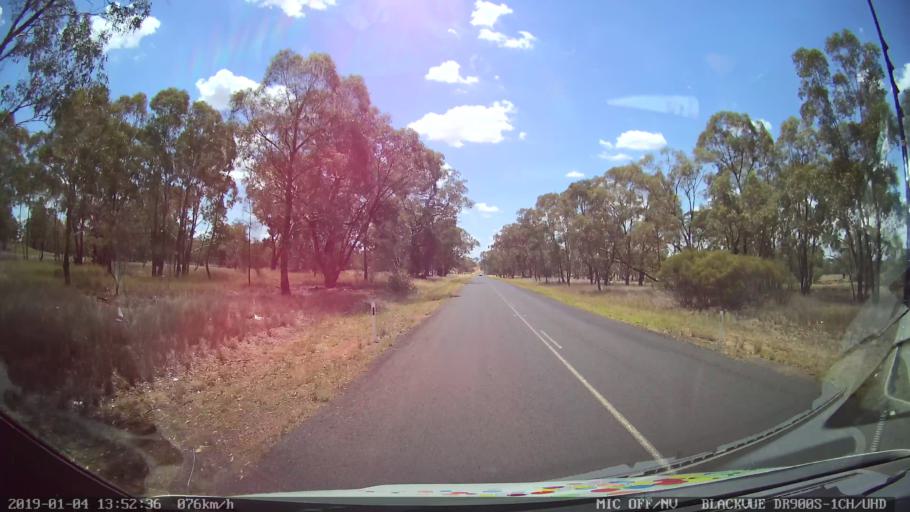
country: AU
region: New South Wales
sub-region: Dubbo Municipality
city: Dubbo
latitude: -32.3925
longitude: 148.5715
